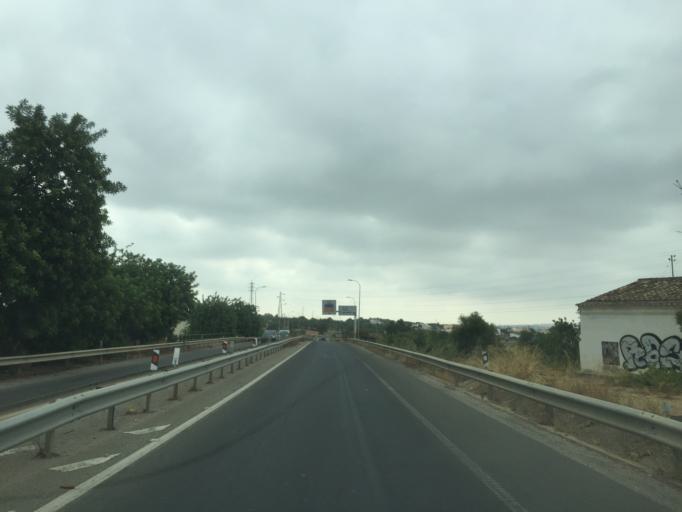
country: PT
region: Faro
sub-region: Faro
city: Santa Barbara de Nexe
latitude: 37.0745
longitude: -7.9813
